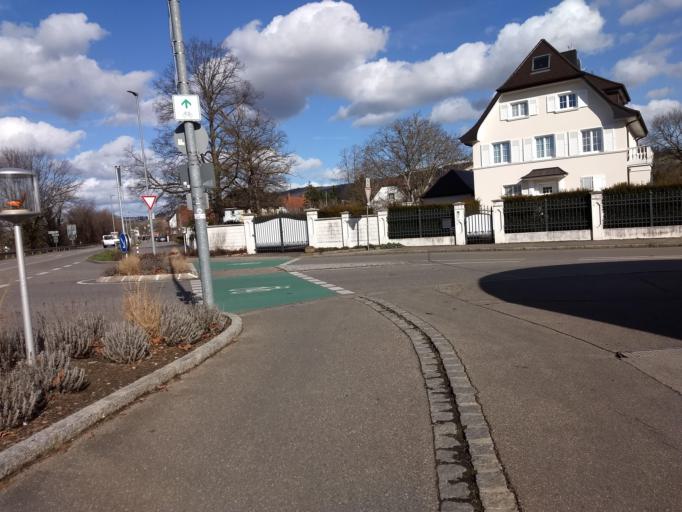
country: DE
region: Baden-Wuerttemberg
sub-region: Freiburg Region
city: Weil am Rhein
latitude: 47.5983
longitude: 7.6124
